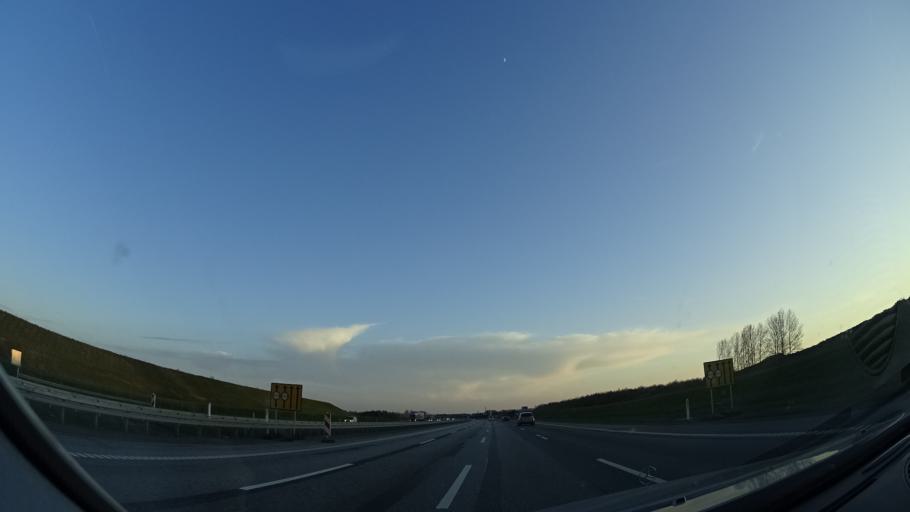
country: DK
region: Zealand
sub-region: Solrod Kommune
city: Solrod Strand
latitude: 55.5660
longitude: 12.2351
